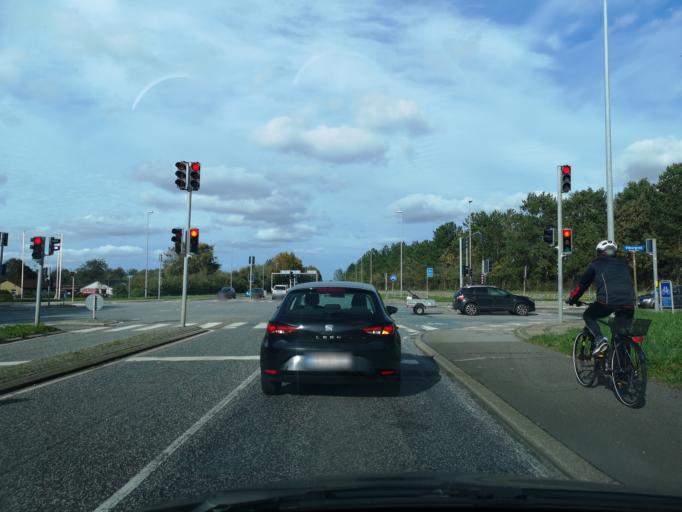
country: DK
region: Central Jutland
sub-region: Holstebro Kommune
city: Holstebro
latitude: 56.3598
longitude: 8.6411
